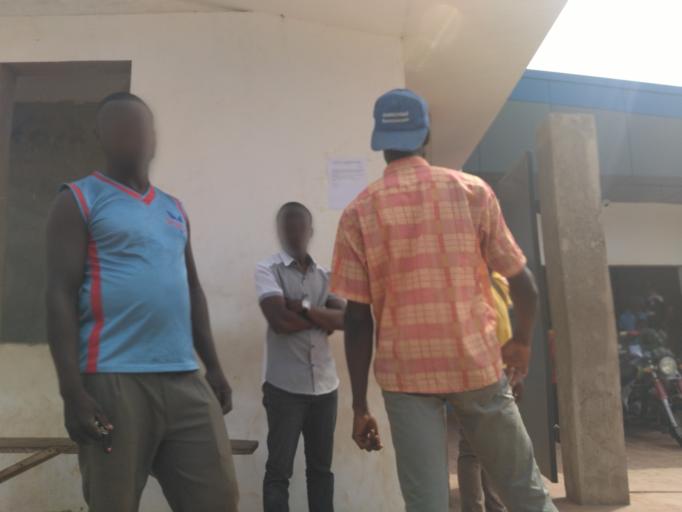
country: GH
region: Ashanti
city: Kumasi
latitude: 6.6733
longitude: -1.6021
